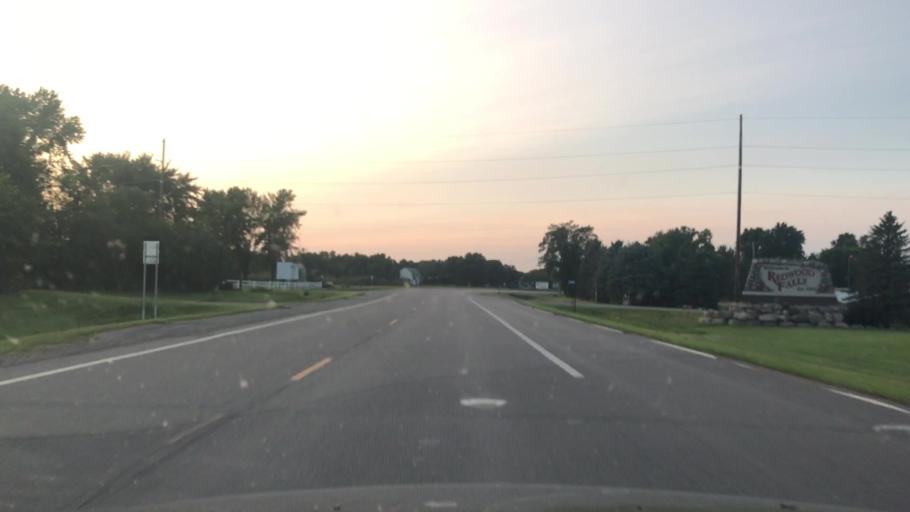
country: US
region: Minnesota
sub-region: Redwood County
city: Redwood Falls
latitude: 44.5245
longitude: -95.1185
